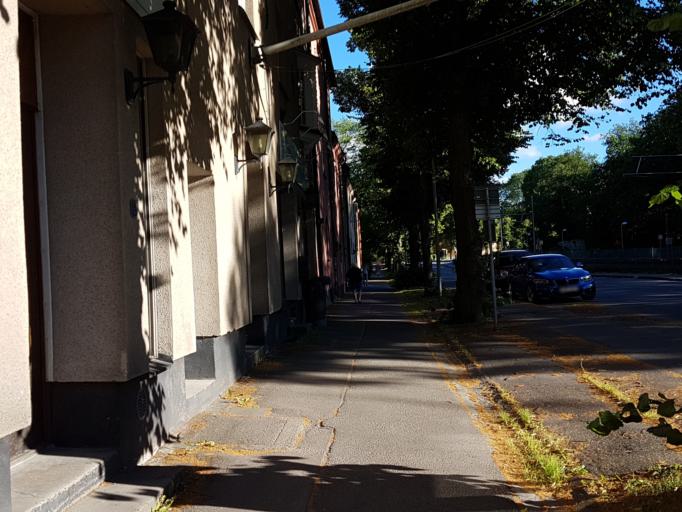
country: SE
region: Stockholm
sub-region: Sundbybergs Kommun
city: Sundbyberg
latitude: 59.3314
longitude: 17.9755
